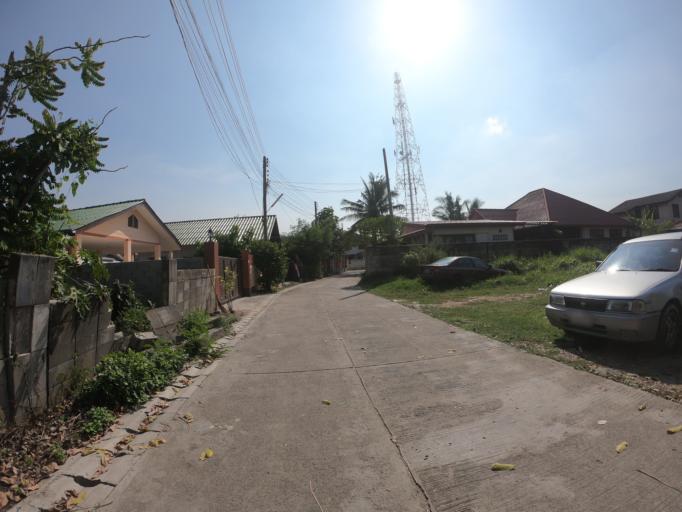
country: TH
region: Chiang Mai
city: Chiang Mai
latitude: 18.8134
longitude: 99.0092
